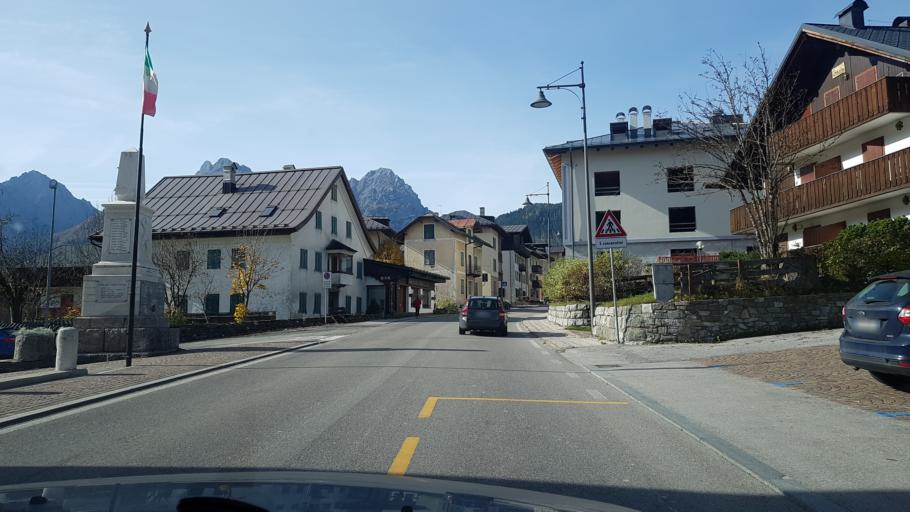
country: IT
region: Veneto
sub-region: Provincia di Belluno
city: Sappada
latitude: 46.5652
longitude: 12.6785
